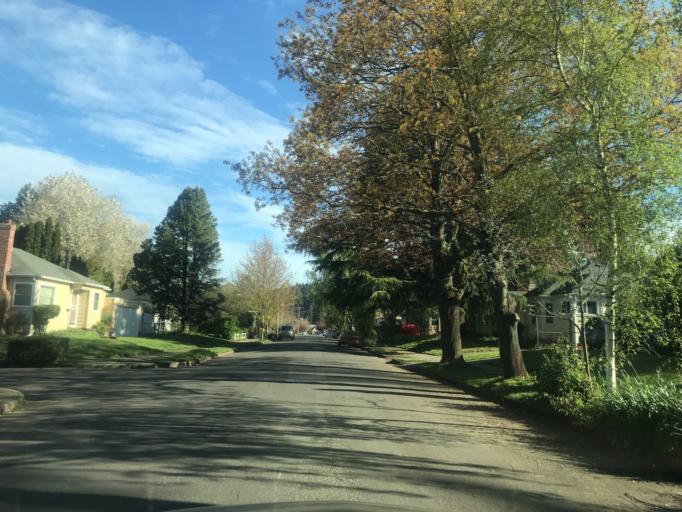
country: US
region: Oregon
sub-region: Multnomah County
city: Lents
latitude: 45.4999
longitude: -122.5966
